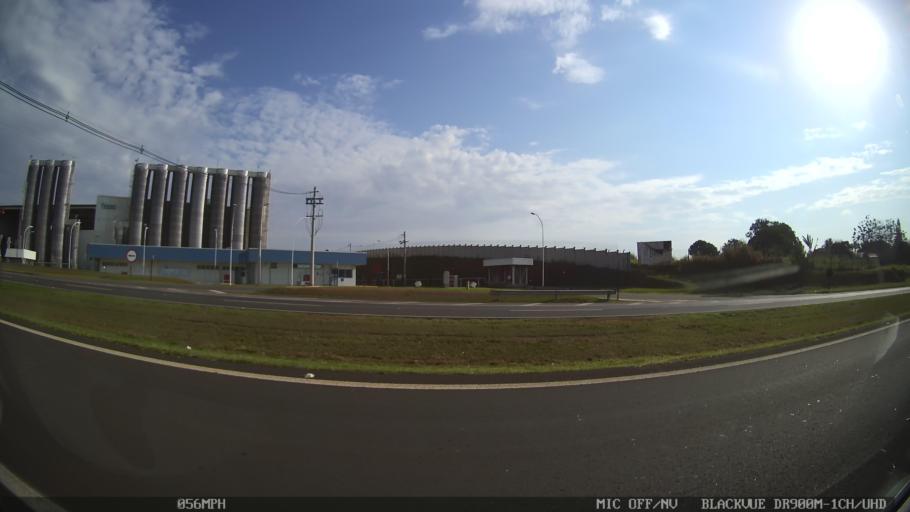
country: BR
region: Sao Paulo
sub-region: Cosmopolis
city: Cosmopolis
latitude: -22.6704
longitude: -47.1627
